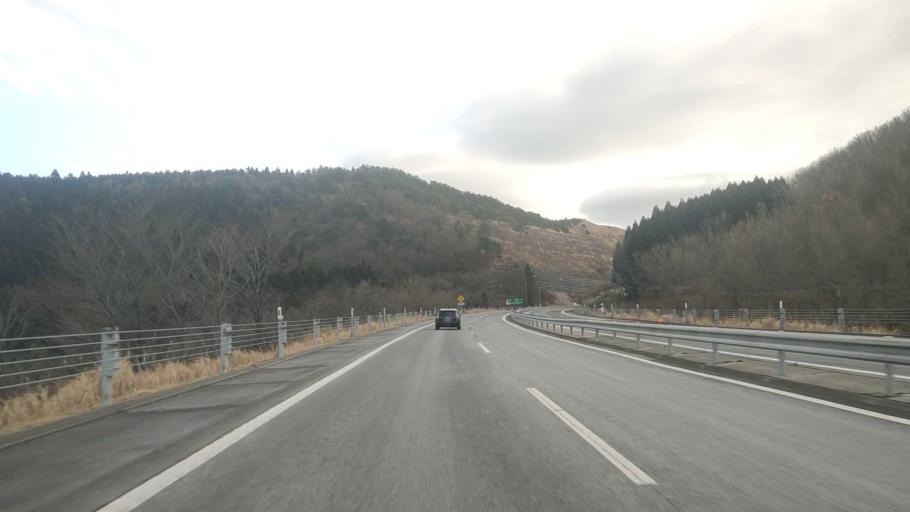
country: JP
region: Oita
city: Beppu
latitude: 33.2947
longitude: 131.3586
